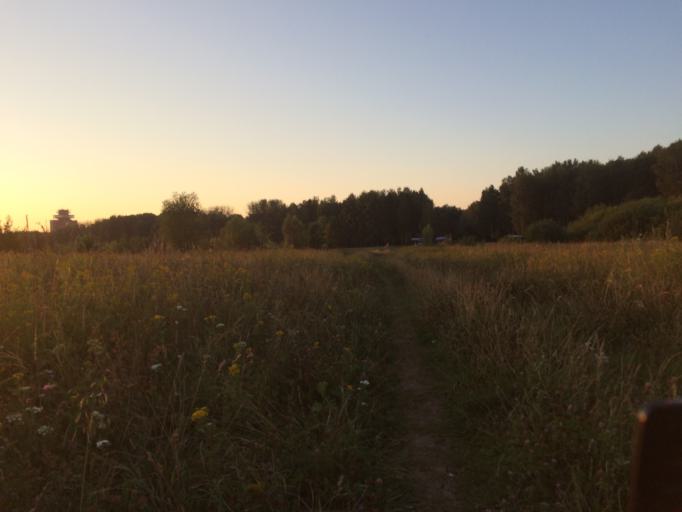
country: RU
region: Mariy-El
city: Yoshkar-Ola
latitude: 56.6205
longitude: 47.9166
